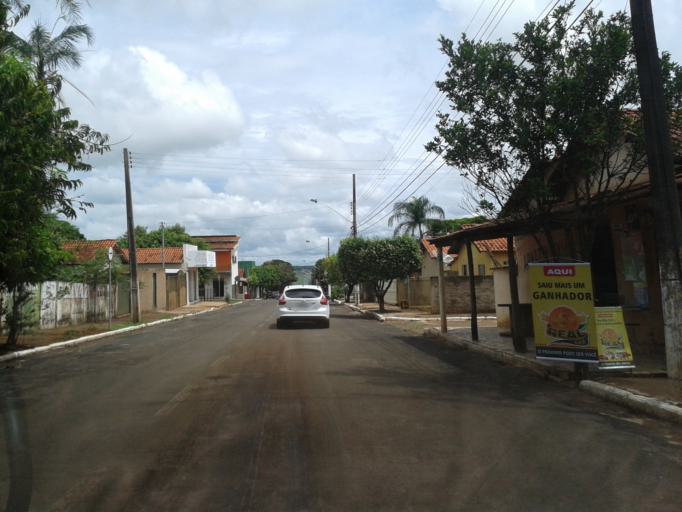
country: BR
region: Goias
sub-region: Buriti Alegre
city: Buriti Alegre
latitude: -18.1319
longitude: -49.0433
